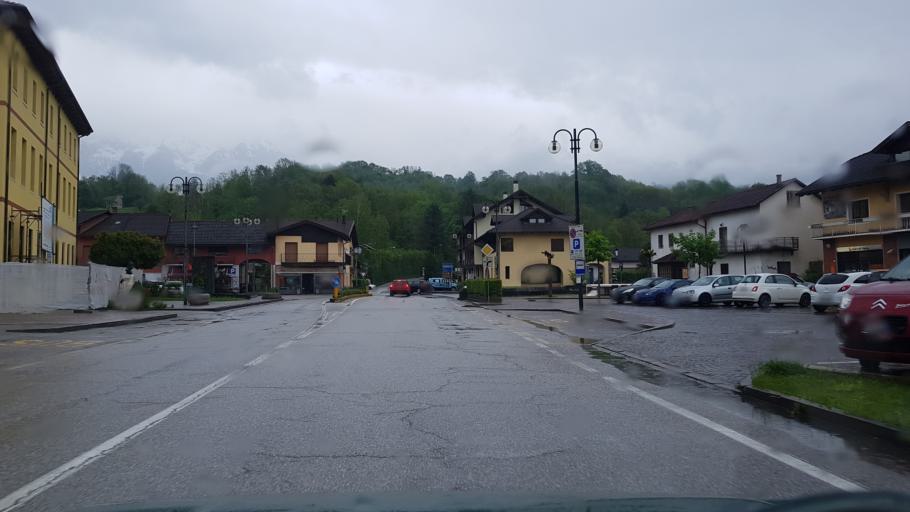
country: IT
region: Veneto
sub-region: Provincia di Belluno
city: Puos d'Alpago
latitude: 46.1415
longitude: 12.3619
